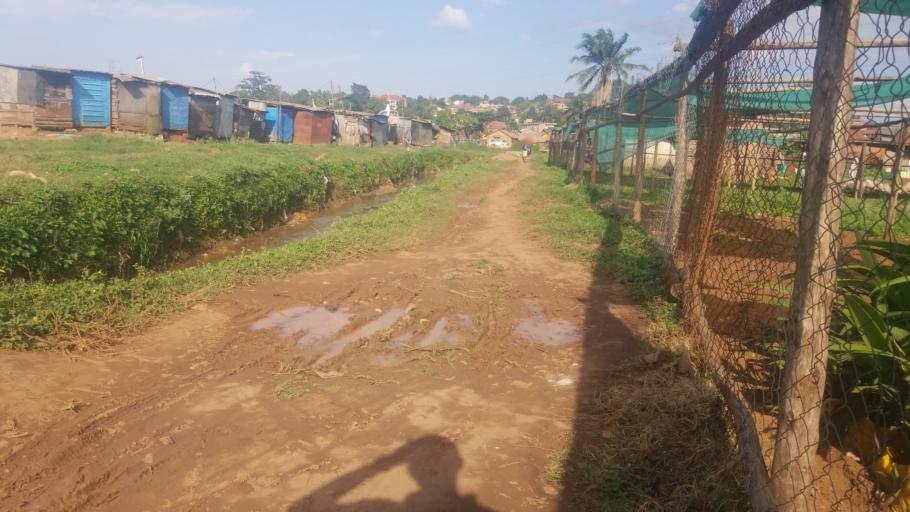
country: UG
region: Central Region
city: Kampala Central Division
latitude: 0.3470
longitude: 32.5561
